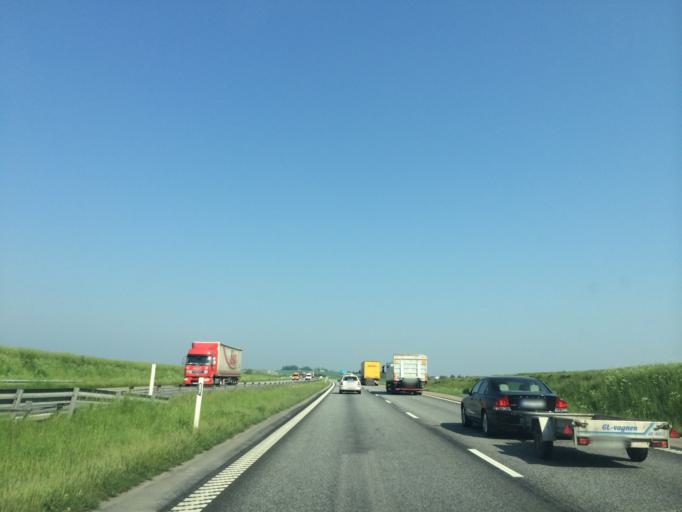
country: SE
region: Skane
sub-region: Landskrona
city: Landskrona
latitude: 55.9118
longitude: 12.8561
